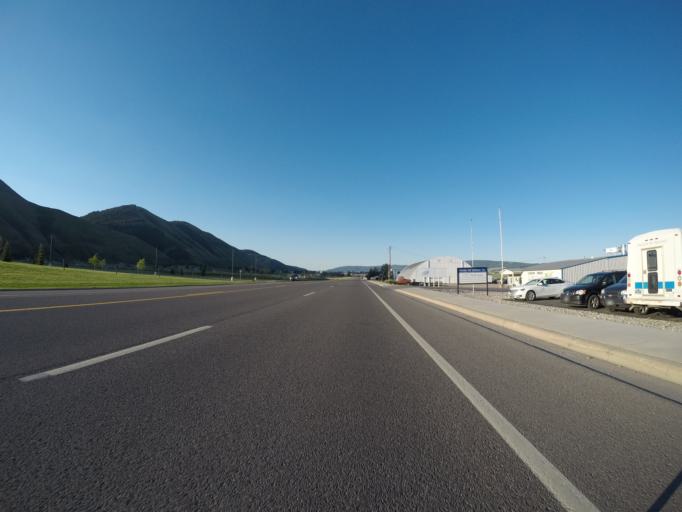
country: US
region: Wyoming
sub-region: Lincoln County
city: Afton
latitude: 42.7119
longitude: -110.9336
